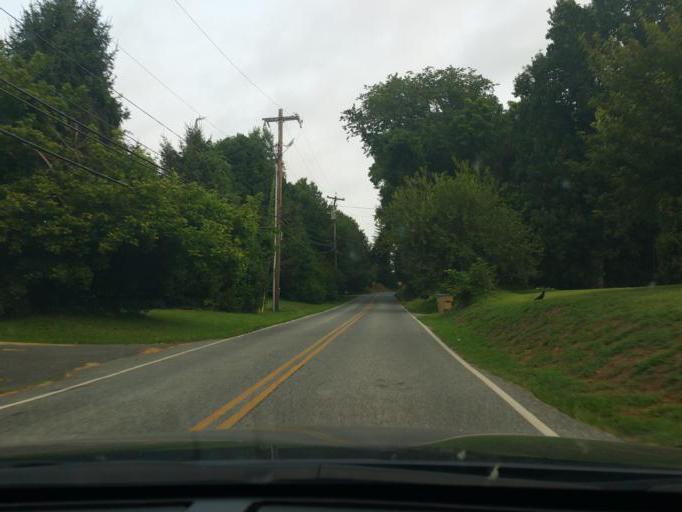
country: US
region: Maryland
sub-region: Cecil County
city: Rising Sun
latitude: 39.6683
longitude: -76.1535
